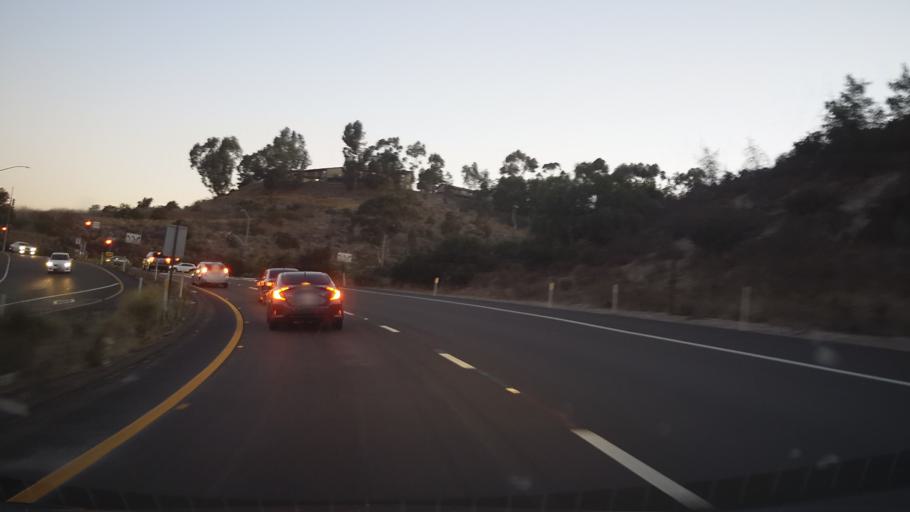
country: US
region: California
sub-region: San Diego County
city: La Mesa
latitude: 32.8106
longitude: -117.1120
